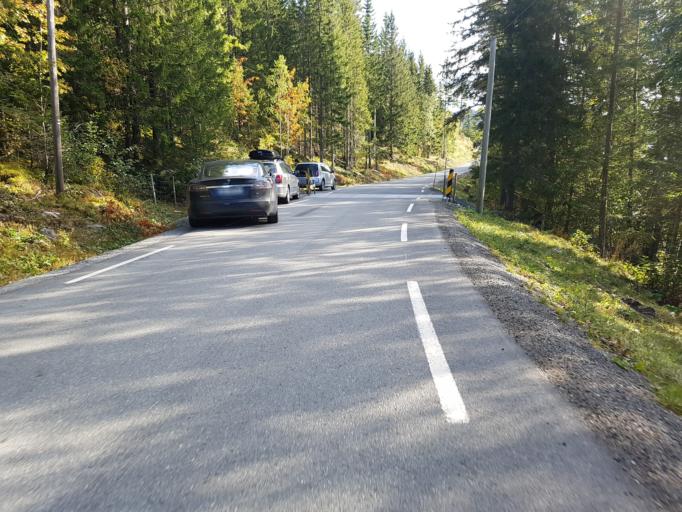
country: NO
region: Sor-Trondelag
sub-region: Malvik
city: Malvik
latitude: 63.3619
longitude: 10.6293
